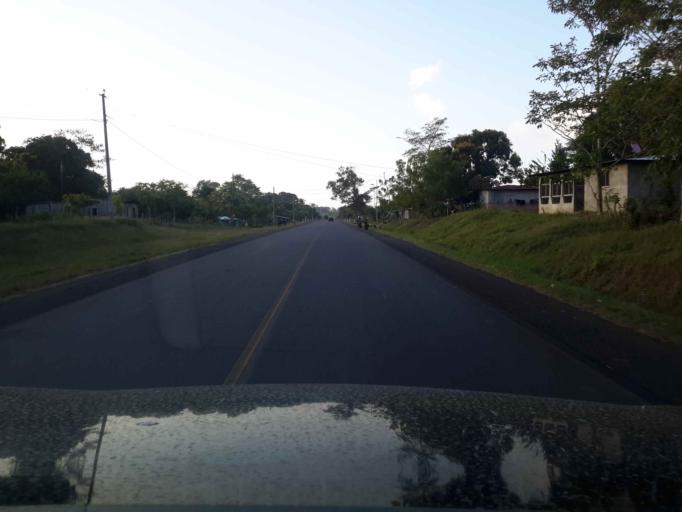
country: NI
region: Rio San Juan
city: San Carlos
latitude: 11.2509
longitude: -84.7044
